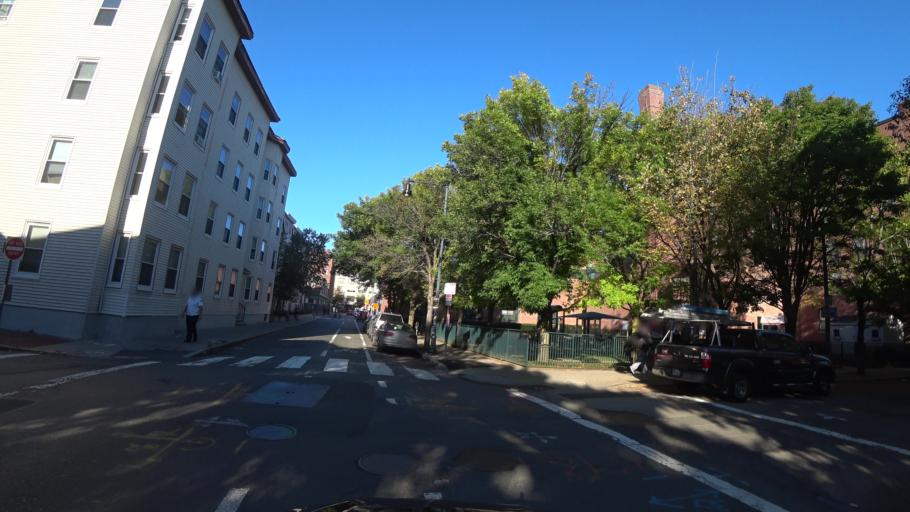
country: US
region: Massachusetts
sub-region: Middlesex County
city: Cambridge
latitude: 42.3628
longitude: -71.1025
